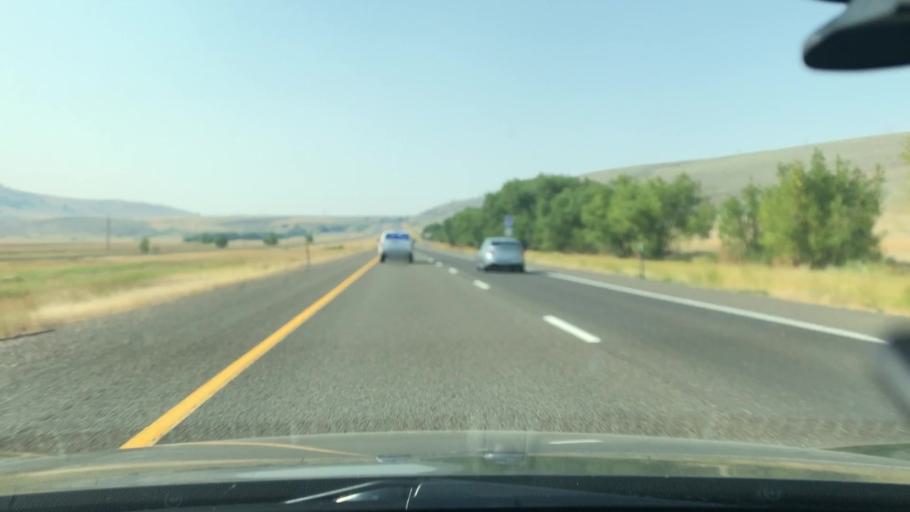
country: US
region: Oregon
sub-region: Union County
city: Union
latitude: 45.1306
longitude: -117.9649
